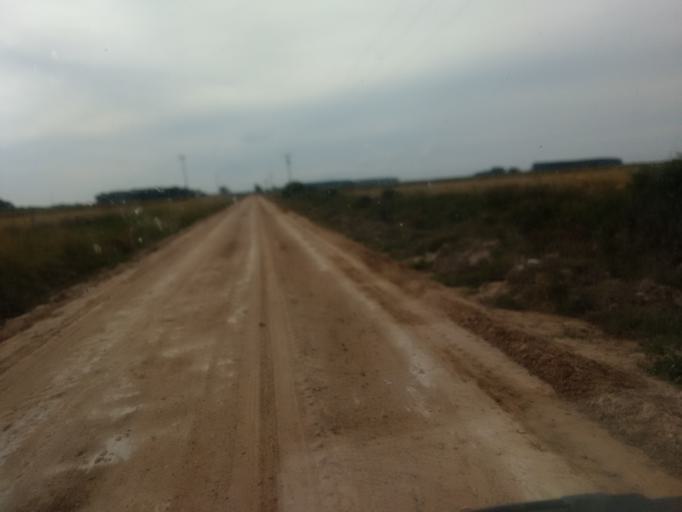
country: BR
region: Rio Grande do Sul
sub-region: Sao Lourenco Do Sul
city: Sao Lourenco do Sul
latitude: -31.1646
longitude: -51.7488
